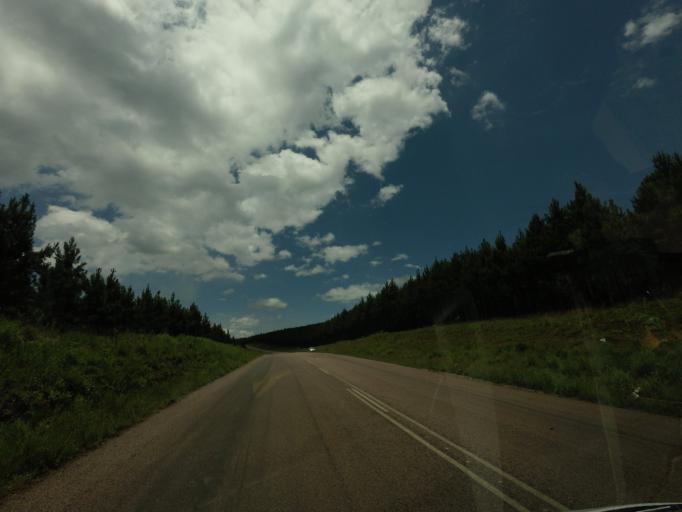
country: ZA
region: Mpumalanga
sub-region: Ehlanzeni District
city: Graksop
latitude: -25.0689
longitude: 30.8061
